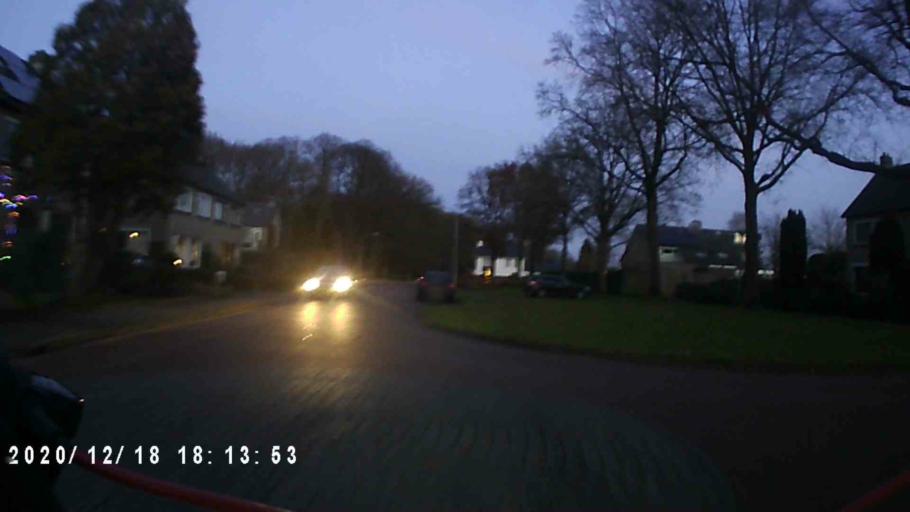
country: NL
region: Groningen
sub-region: Gemeente Haren
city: Haren
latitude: 53.1478
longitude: 6.5590
